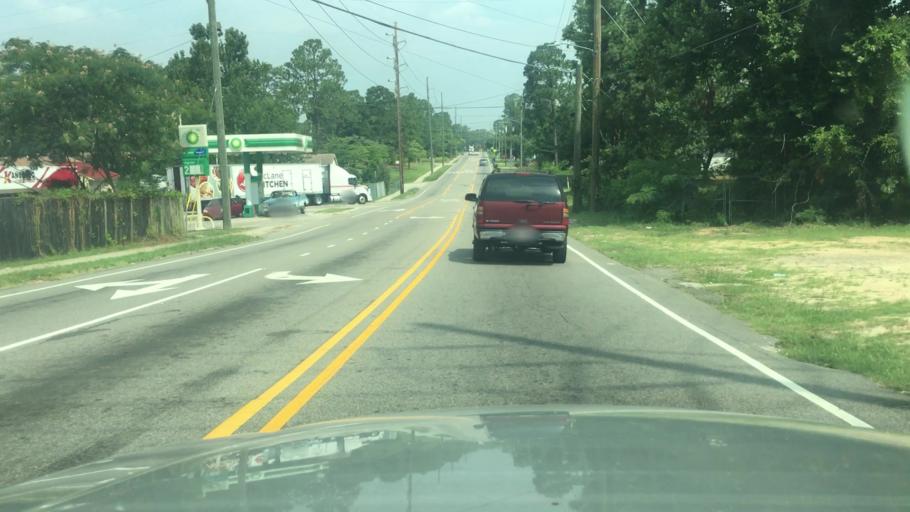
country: US
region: North Carolina
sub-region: Cumberland County
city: Hope Mills
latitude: 35.0259
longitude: -78.9425
